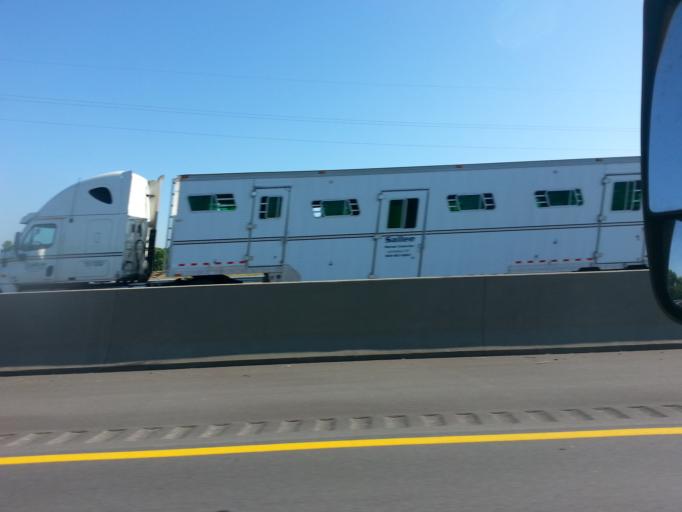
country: US
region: Kentucky
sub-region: Shelby County
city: Simpsonville
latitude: 38.2010
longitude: -85.3060
